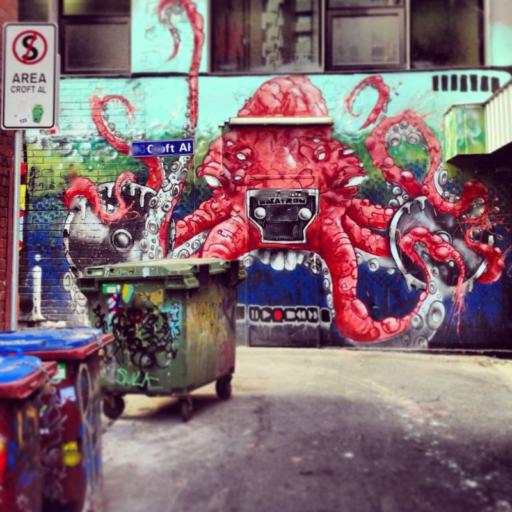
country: AU
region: Victoria
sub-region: Melbourne
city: Melbourne
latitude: -37.8116
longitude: 144.9689
